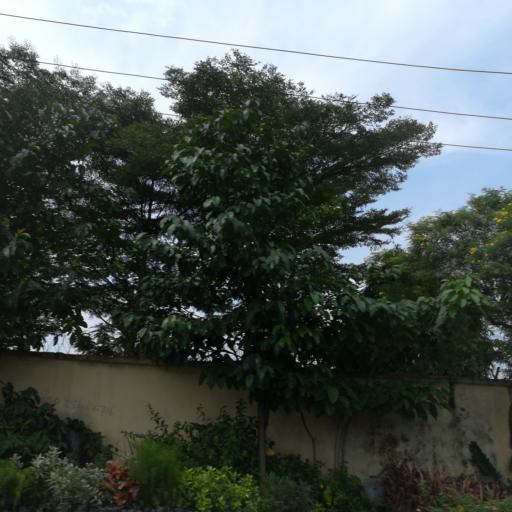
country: NG
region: Rivers
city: Port Harcourt
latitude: 4.8536
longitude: 7.0209
